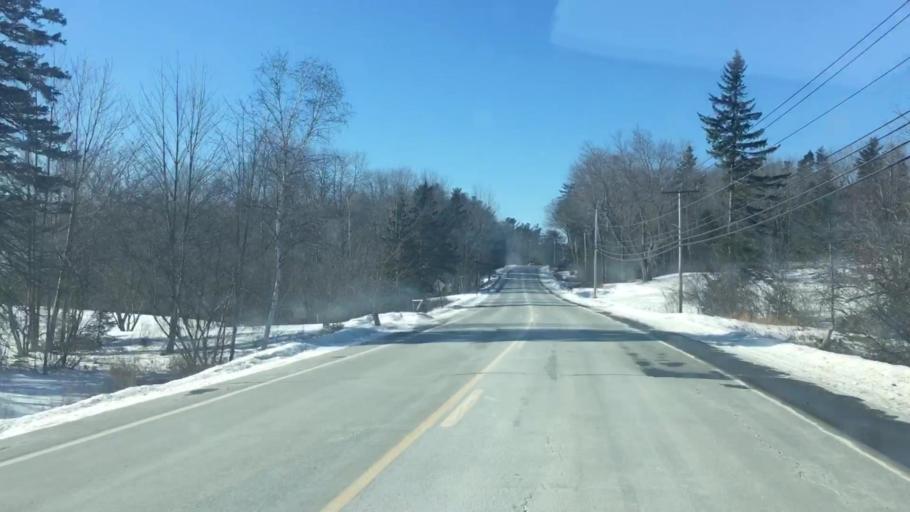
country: US
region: Maine
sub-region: Hancock County
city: Surry
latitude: 44.4948
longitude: -68.4717
